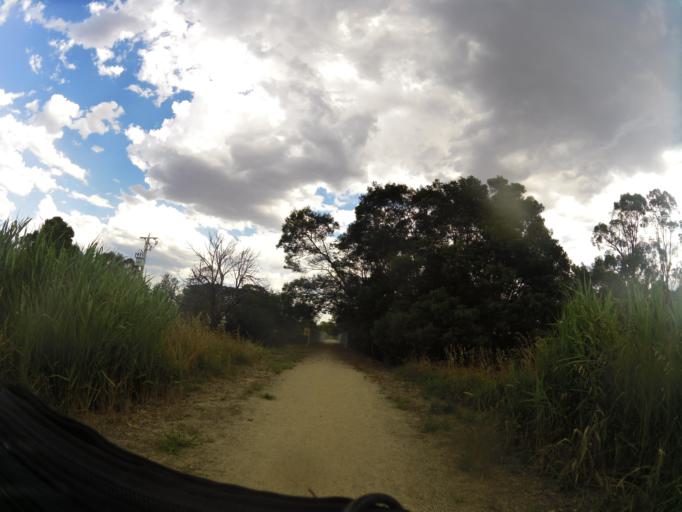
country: AU
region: Victoria
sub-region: Wellington
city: Heyfield
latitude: -38.0095
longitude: 146.6970
